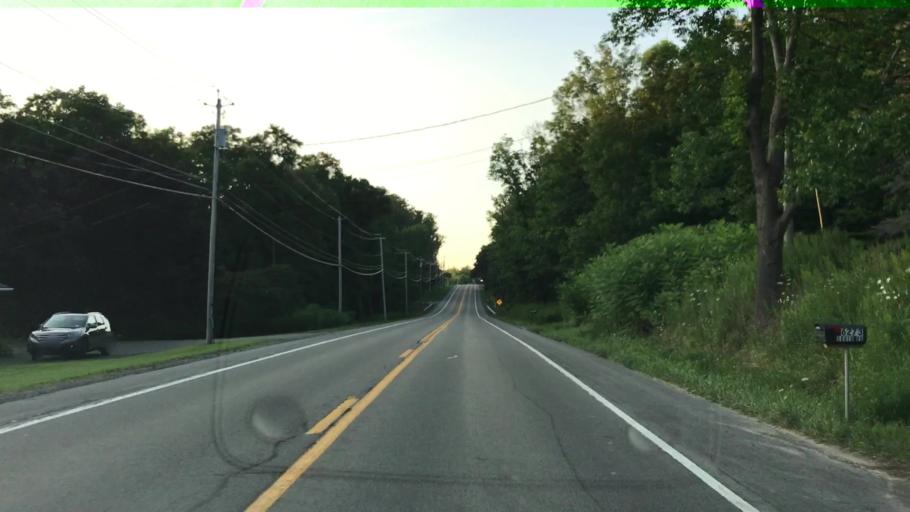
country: US
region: New York
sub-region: Chautauqua County
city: Mayville
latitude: 42.2548
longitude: -79.4666
